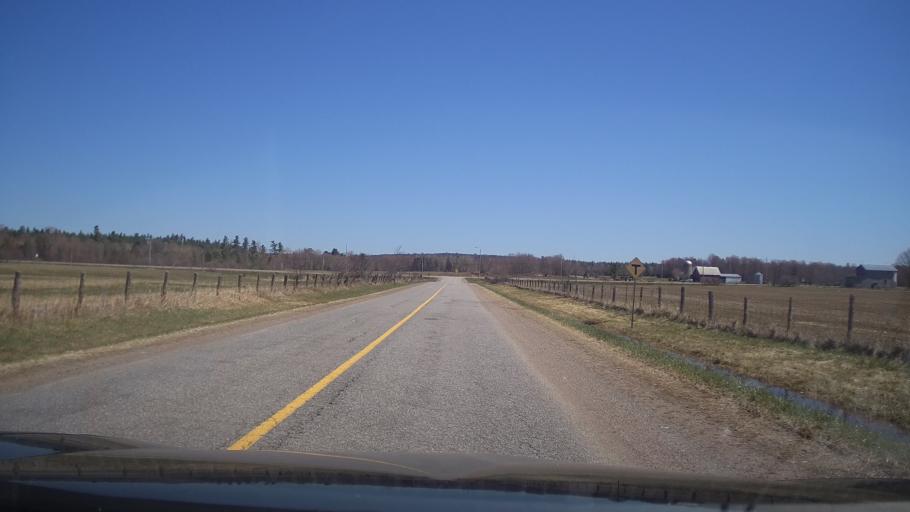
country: CA
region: Quebec
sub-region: Outaouais
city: Shawville
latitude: 45.5491
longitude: -76.3855
